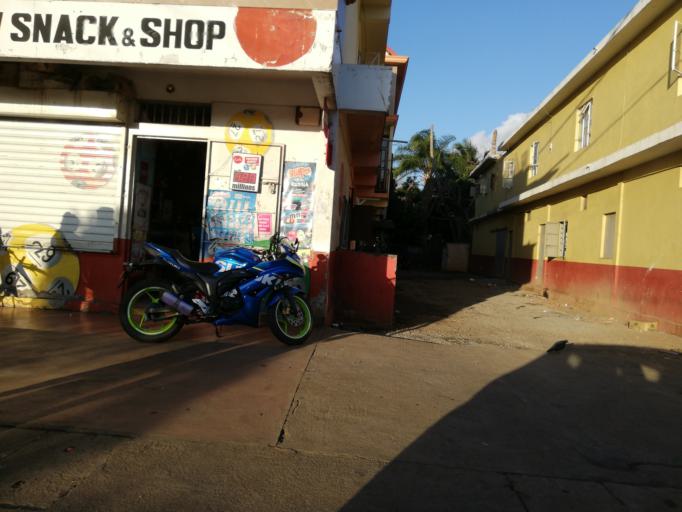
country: MU
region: Pamplemousses
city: Terre Rouge
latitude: -20.1252
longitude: 57.5319
